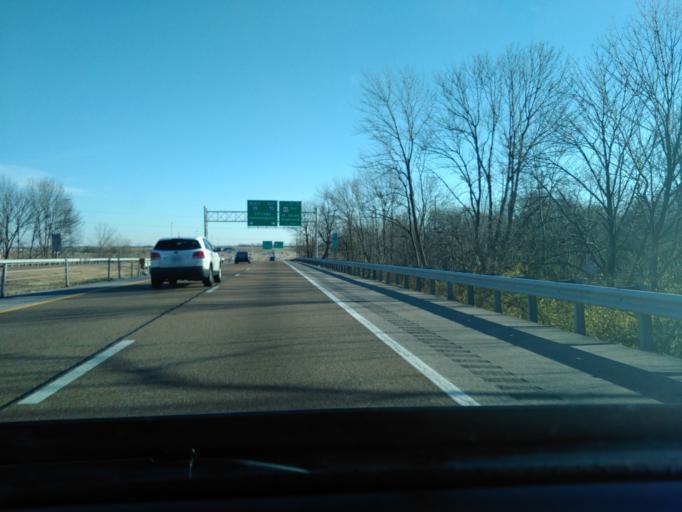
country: US
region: Illinois
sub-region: Madison County
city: Maryville
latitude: 38.7142
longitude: -89.9278
